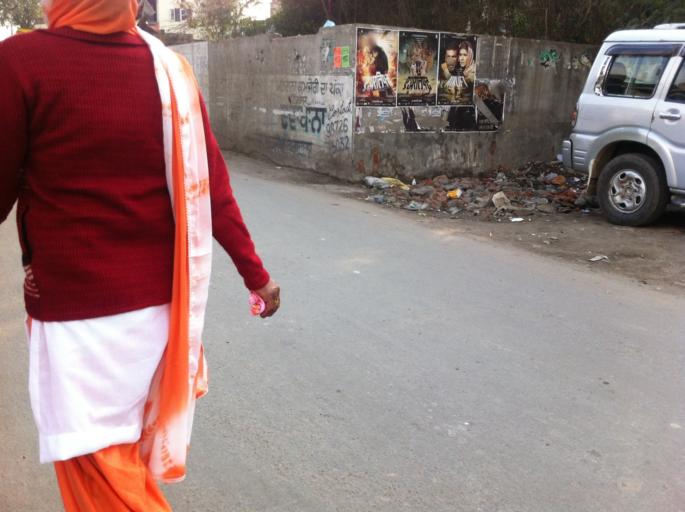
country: IN
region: Punjab
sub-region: Kapurthala
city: Phagwara
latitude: 31.2181
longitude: 75.7735
